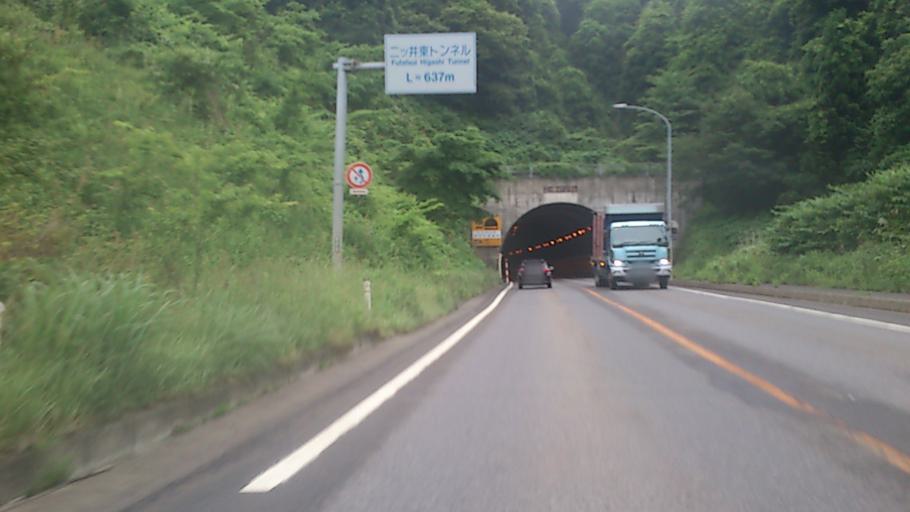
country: JP
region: Akita
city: Takanosu
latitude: 40.2186
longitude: 140.2410
